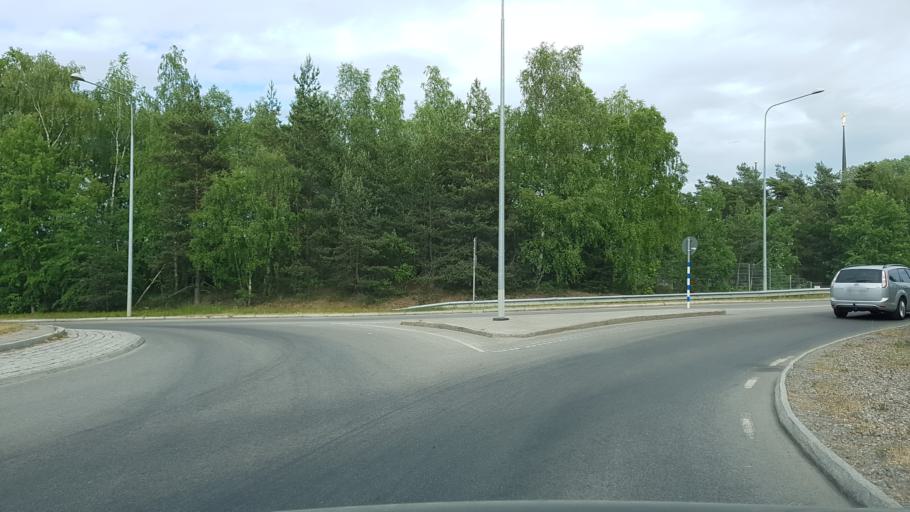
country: SE
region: Stockholm
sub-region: Haninge Kommun
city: Jordbro
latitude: 59.1249
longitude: 18.1067
